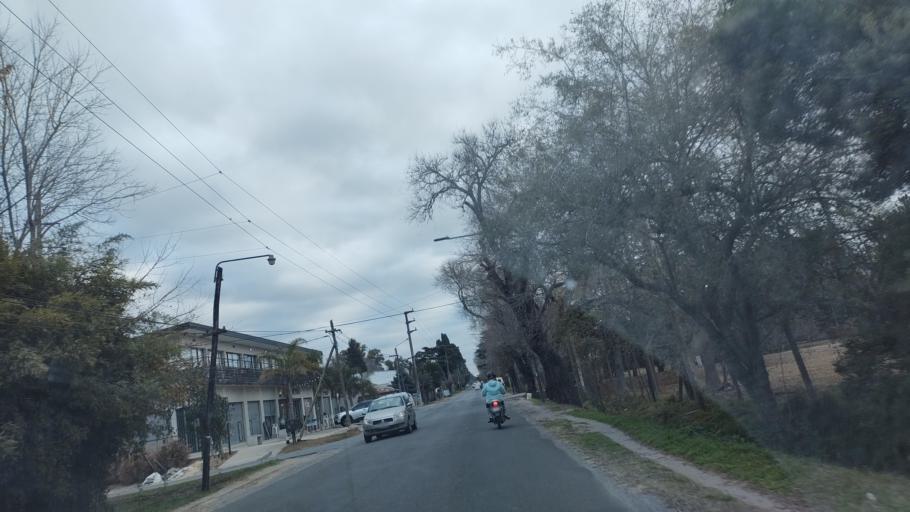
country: AR
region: Buenos Aires
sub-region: Partido de La Plata
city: La Plata
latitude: -34.8661
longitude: -58.0938
